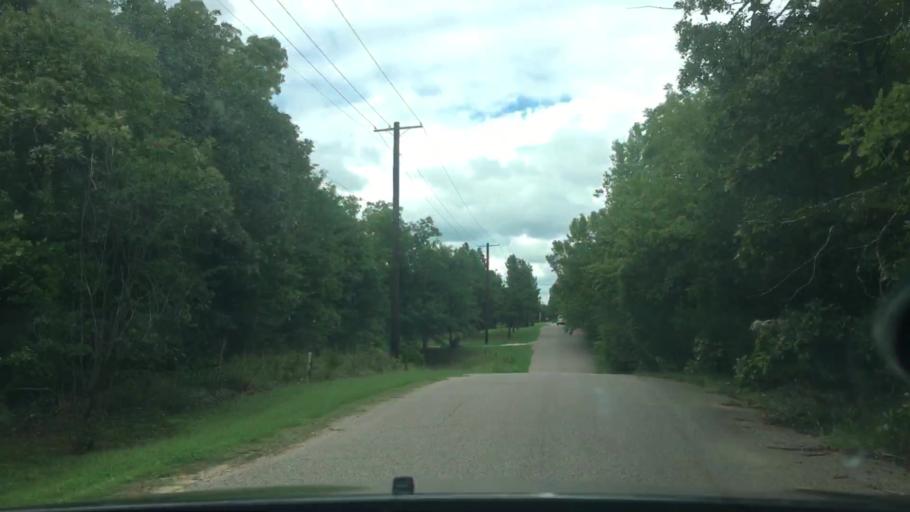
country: US
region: Oklahoma
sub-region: Pontotoc County
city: Ada
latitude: 34.7537
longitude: -96.6524
